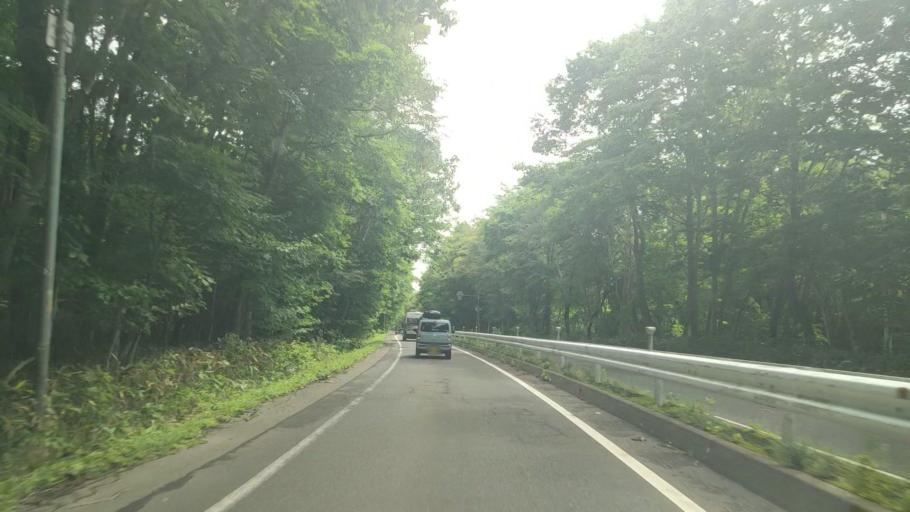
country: JP
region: Hokkaido
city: Chitose
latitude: 42.7842
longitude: 141.4411
